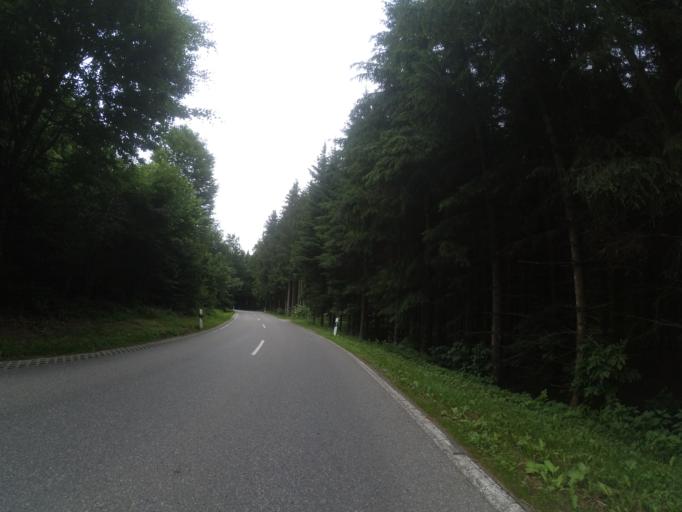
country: DE
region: Bavaria
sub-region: Swabia
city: Gestratz
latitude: 47.6965
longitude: 9.9718
